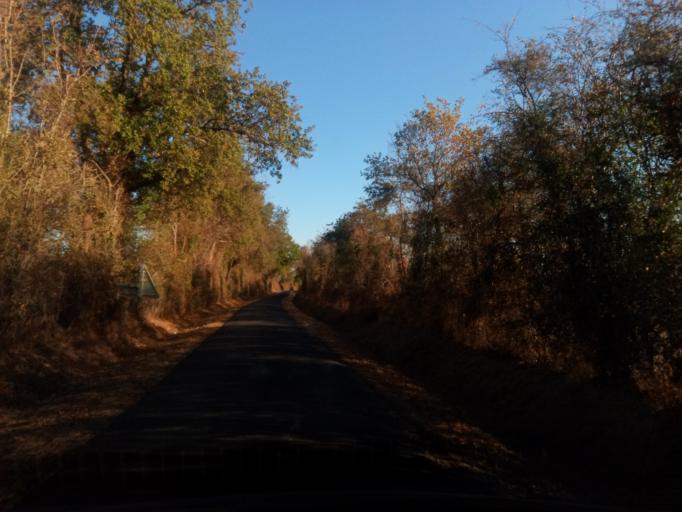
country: FR
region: Poitou-Charentes
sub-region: Departement de la Vienne
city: Saulge
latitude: 46.4023
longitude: 0.8689
